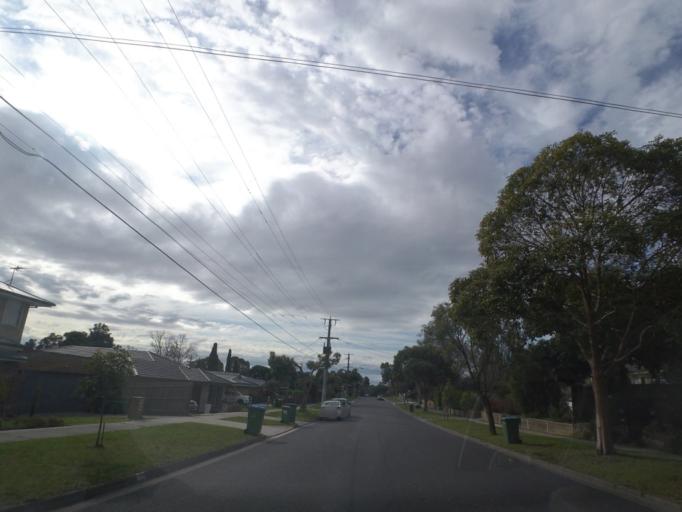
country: AU
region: Victoria
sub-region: Maroondah
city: Heathmont
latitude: -37.8305
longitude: 145.2373
